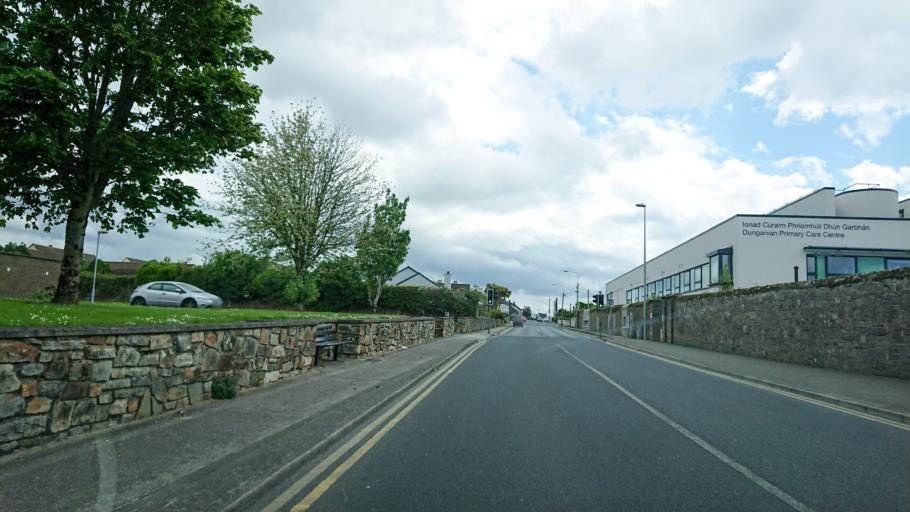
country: IE
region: Munster
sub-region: Waterford
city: Dungarvan
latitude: 52.0885
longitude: -7.6365
